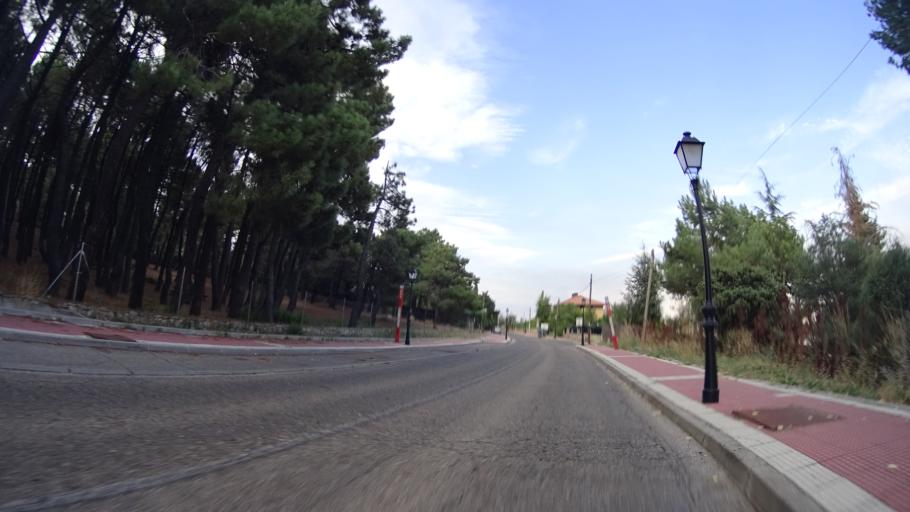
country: ES
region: Madrid
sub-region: Provincia de Madrid
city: Becerril de la Sierra
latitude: 40.7131
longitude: -4.0006
